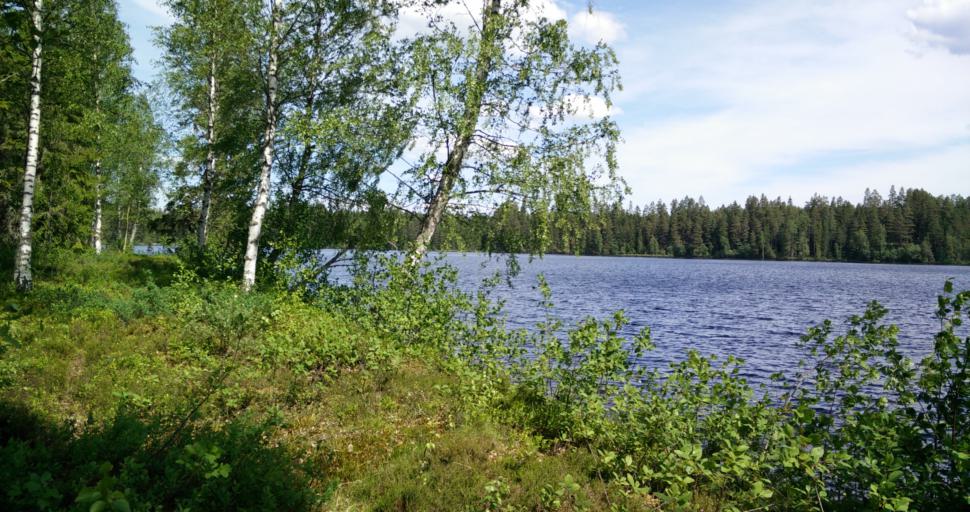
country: SE
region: Vaermland
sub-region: Hagfors Kommun
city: Hagfors
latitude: 59.9936
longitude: 13.5731
